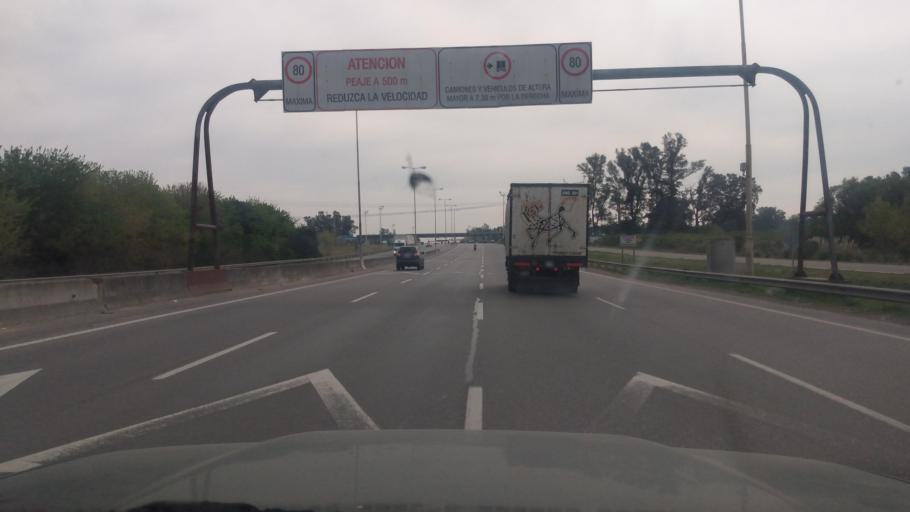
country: AR
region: Buenos Aires
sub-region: Partido de Pilar
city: Pilar
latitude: -34.4067
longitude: -59.0098
